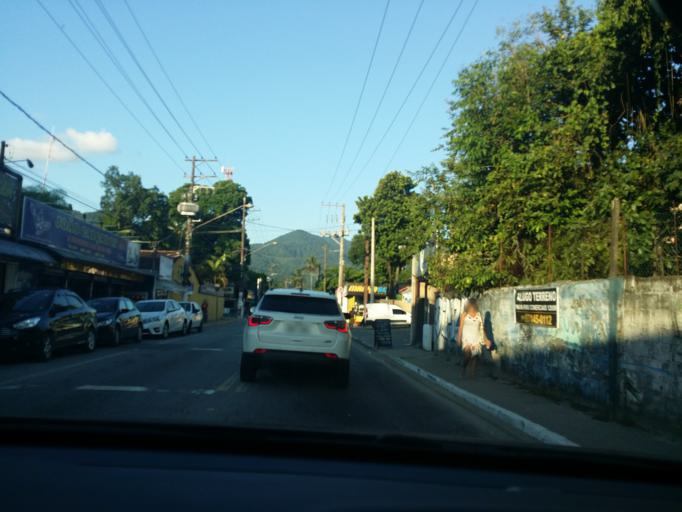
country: BR
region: Sao Paulo
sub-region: Sao Sebastiao
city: Sao Sebastiao
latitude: -23.7851
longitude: -45.6240
